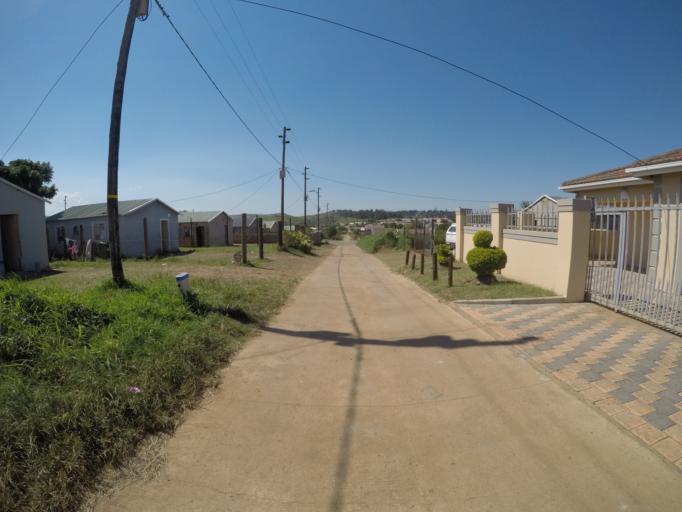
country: ZA
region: KwaZulu-Natal
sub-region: uThungulu District Municipality
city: Empangeni
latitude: -28.7684
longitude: 31.8784
